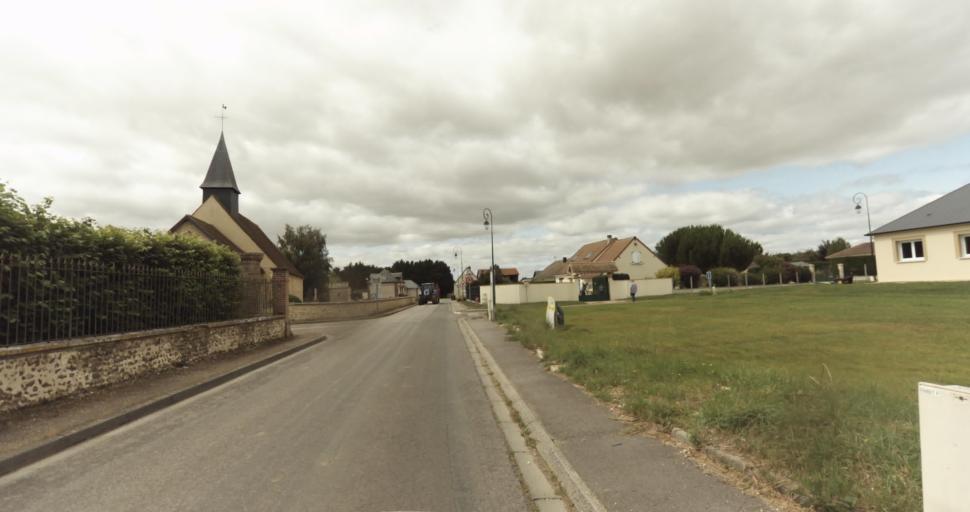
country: FR
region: Haute-Normandie
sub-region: Departement de l'Eure
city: Evreux
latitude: 48.9142
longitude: 1.2095
